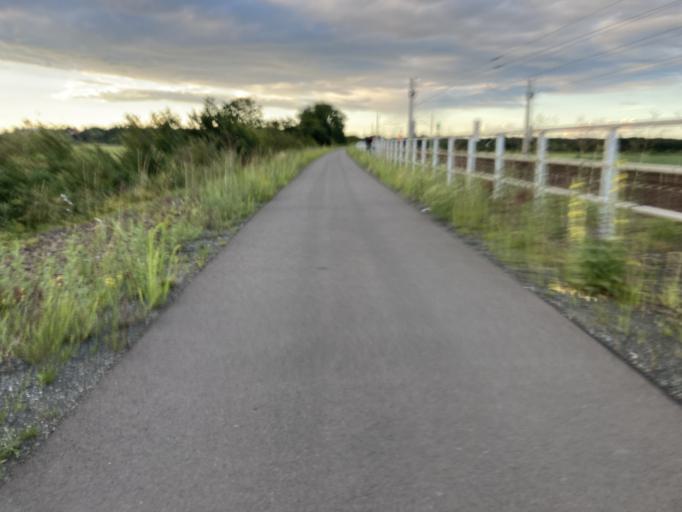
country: DE
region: Lower Saxony
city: Verden
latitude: 52.9019
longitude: 9.2392
